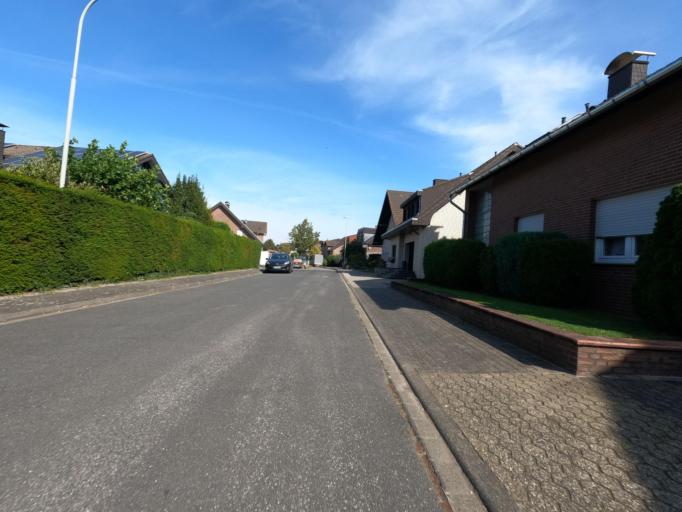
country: DE
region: North Rhine-Westphalia
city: Siersdorf
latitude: 50.9251
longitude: 6.2538
